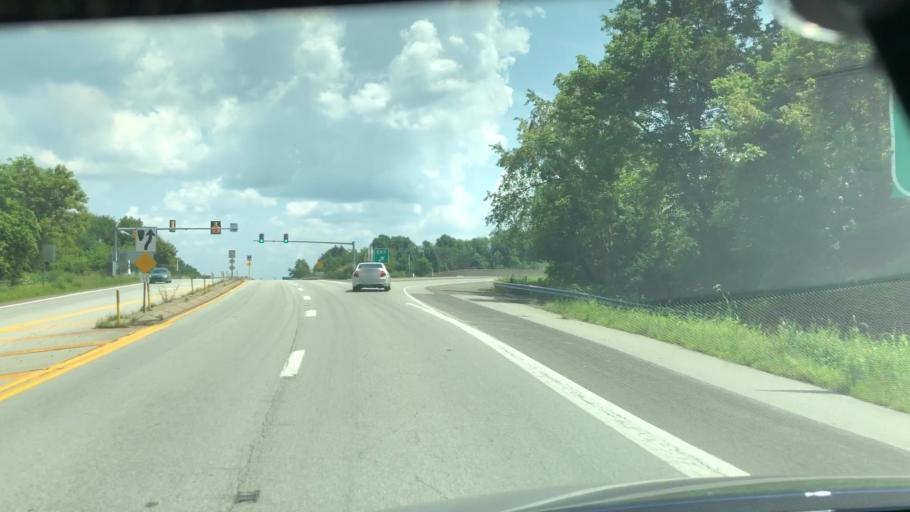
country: US
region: Pennsylvania
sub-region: Armstrong County
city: Freeport
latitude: 40.6921
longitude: -79.7127
